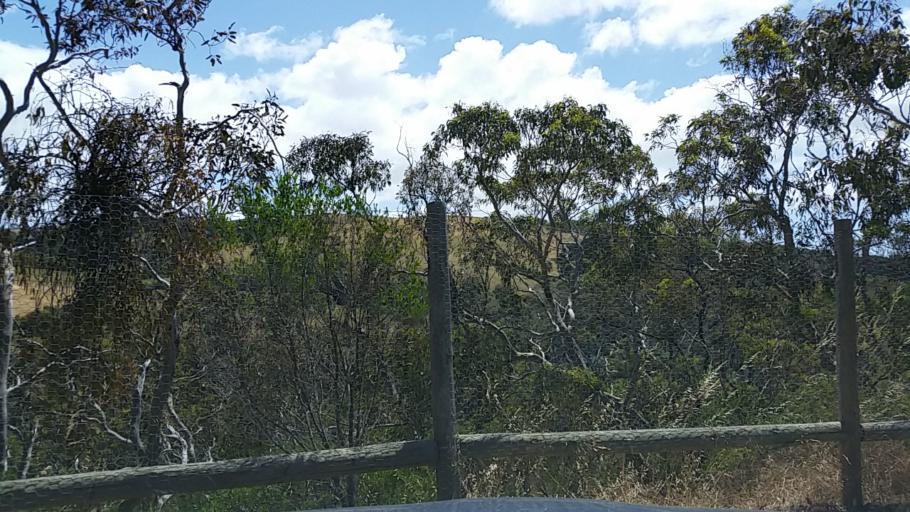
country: AU
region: South Australia
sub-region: Alexandrina
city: Mount Compass
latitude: -35.4422
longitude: 138.5843
